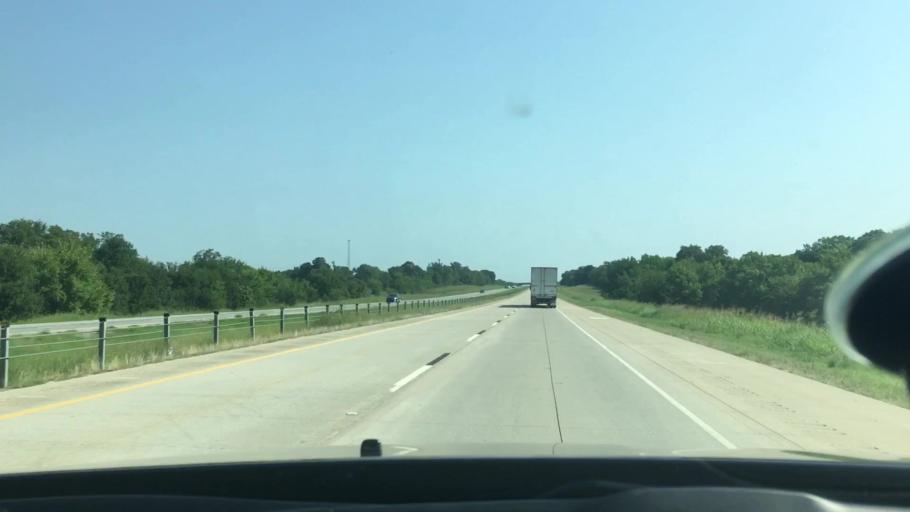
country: US
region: Oklahoma
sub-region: Bryan County
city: Durant
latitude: 34.0650
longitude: -96.3472
